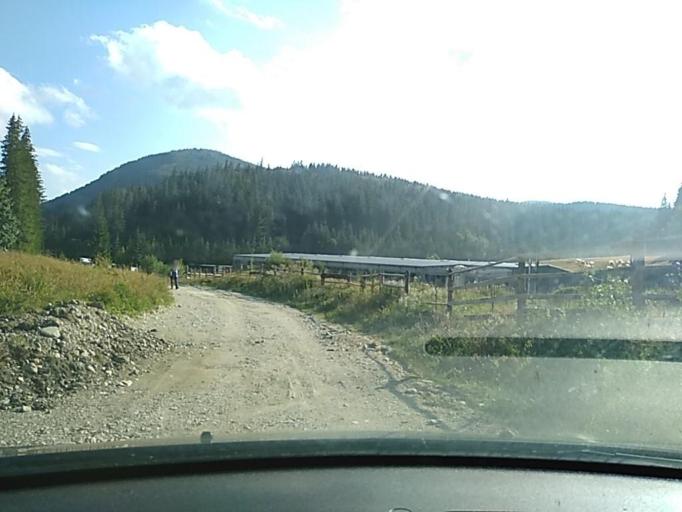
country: RO
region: Brasov
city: Crivina
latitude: 45.4843
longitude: 25.9207
